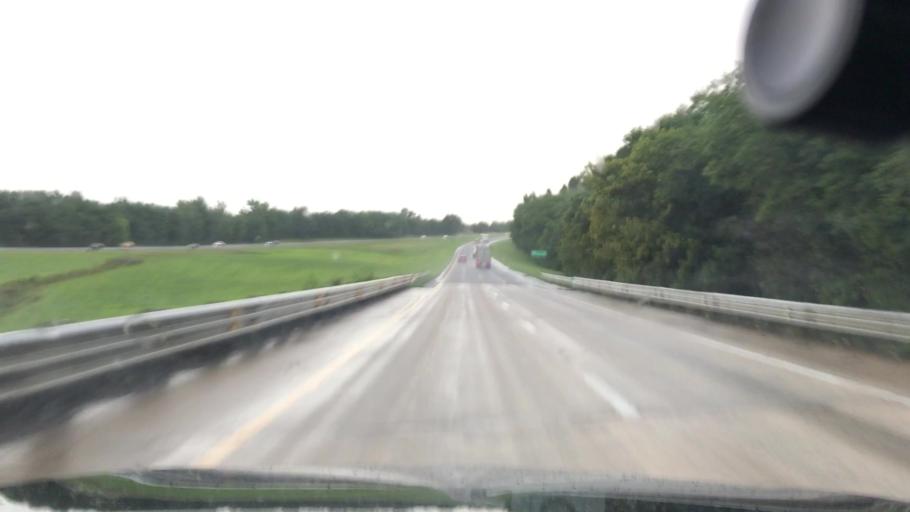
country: US
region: North Carolina
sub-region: Iredell County
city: Statesville
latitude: 35.9281
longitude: -80.8552
